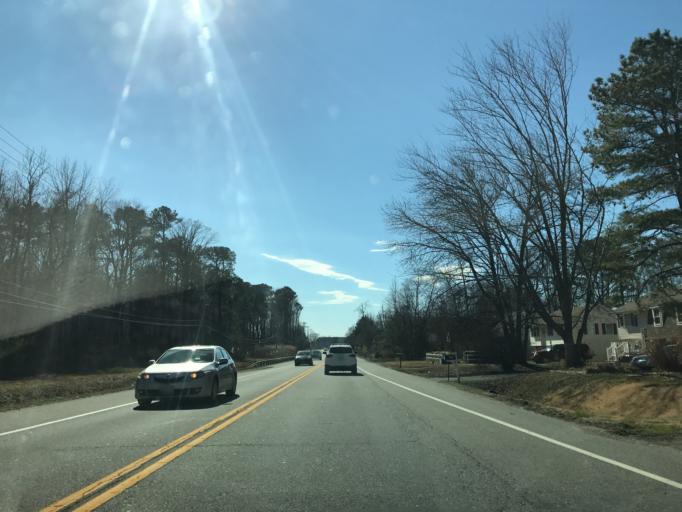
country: US
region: Maryland
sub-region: Queen Anne's County
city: Stevensville
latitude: 38.9690
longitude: -76.3311
